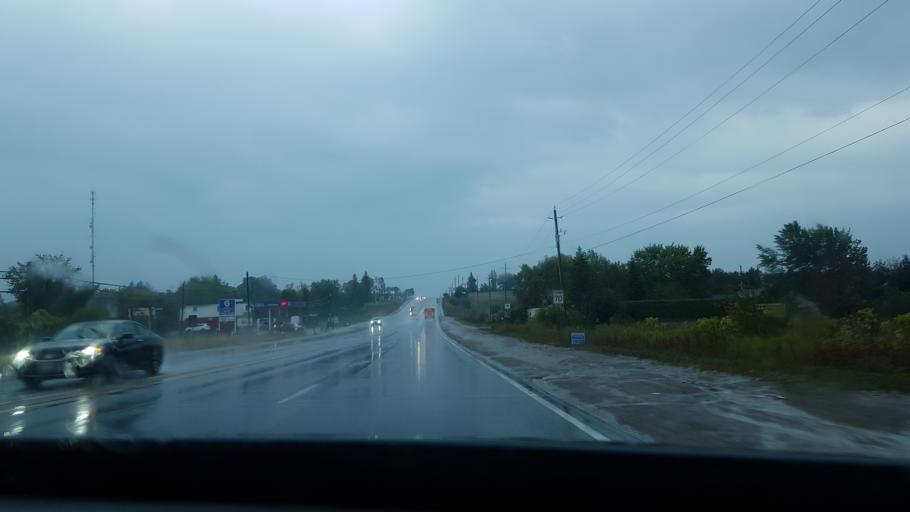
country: CA
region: Ontario
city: Peterborough
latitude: 44.3479
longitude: -78.3606
